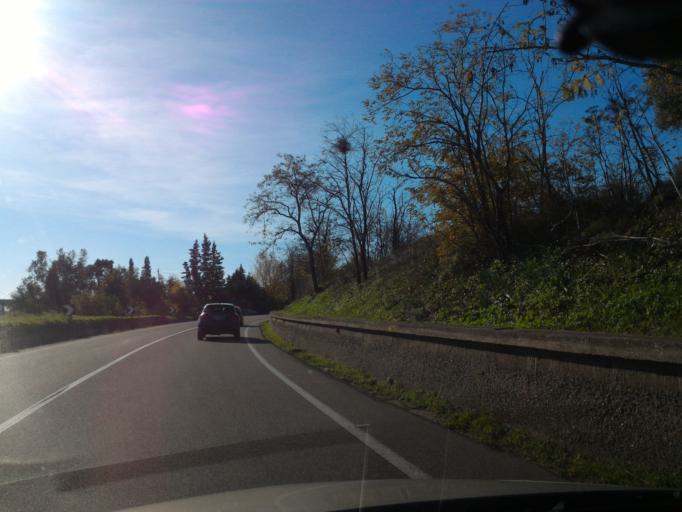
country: IT
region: Calabria
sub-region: Provincia di Crotone
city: Tronca
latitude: 39.2105
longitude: 17.1097
